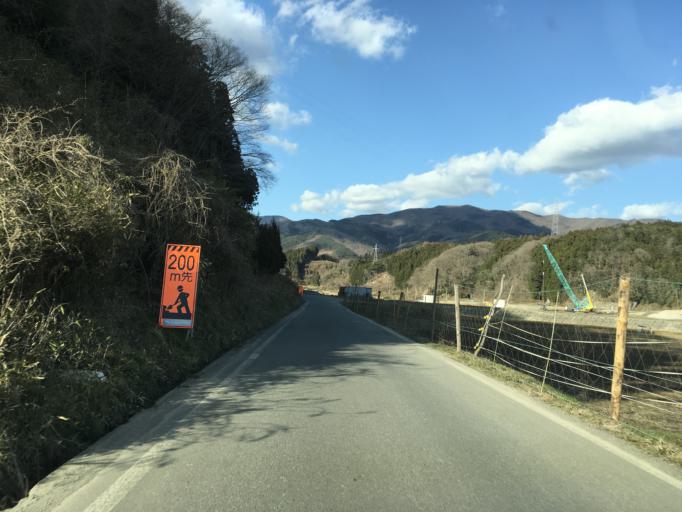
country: JP
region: Iwate
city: Ofunato
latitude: 39.0207
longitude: 141.6156
